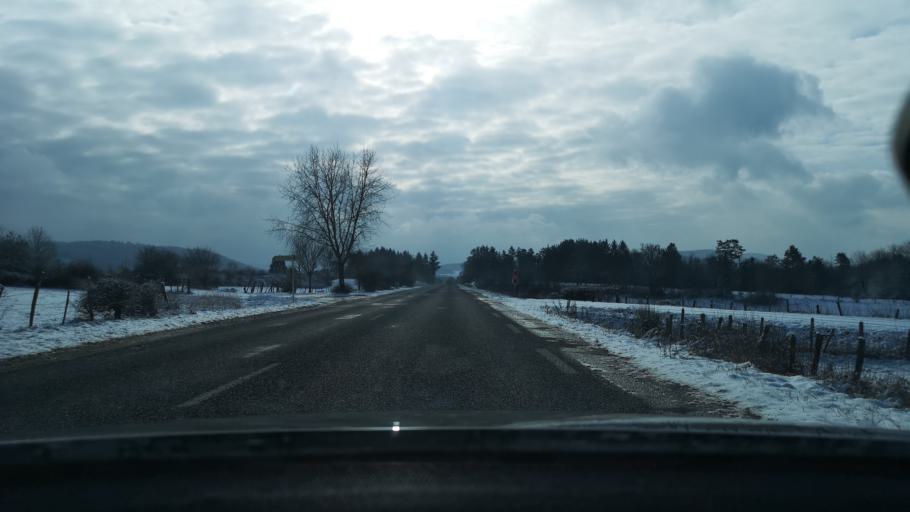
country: FR
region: Franche-Comte
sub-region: Departement du Jura
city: Orgelet
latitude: 46.5544
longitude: 5.5964
